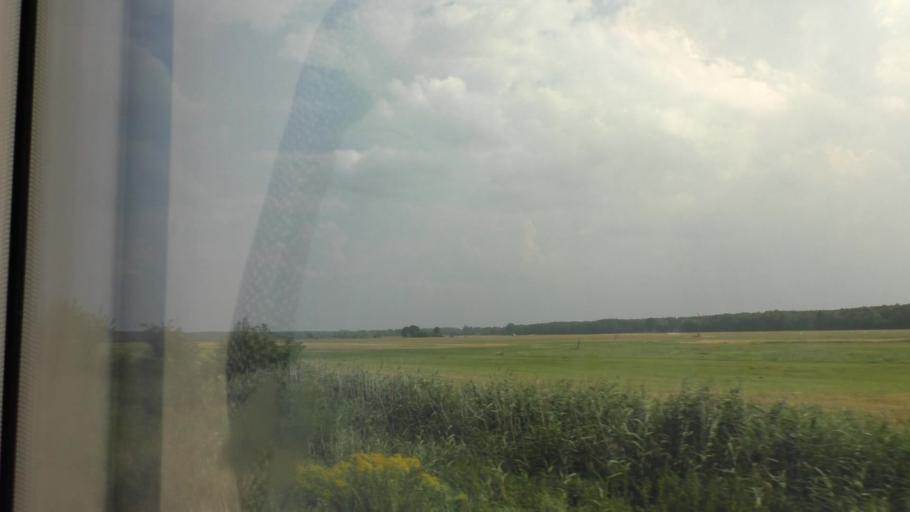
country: DE
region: Brandenburg
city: Spreenhagen
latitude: 52.2870
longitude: 13.8022
